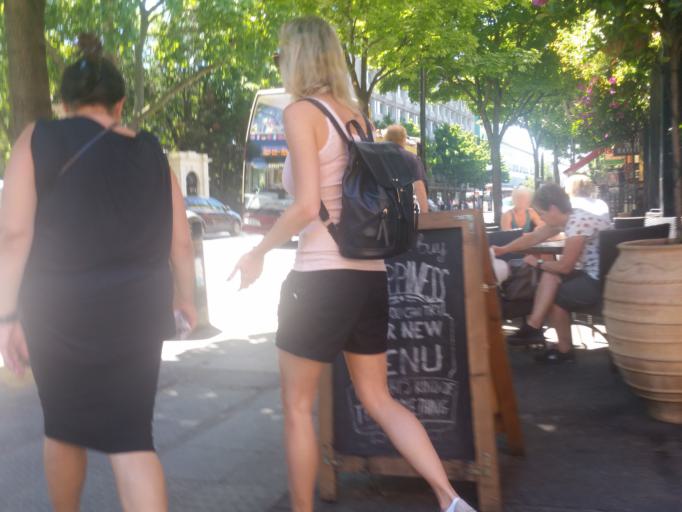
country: GB
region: England
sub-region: Greater London
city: Bayswater
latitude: 51.5099
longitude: -0.1920
